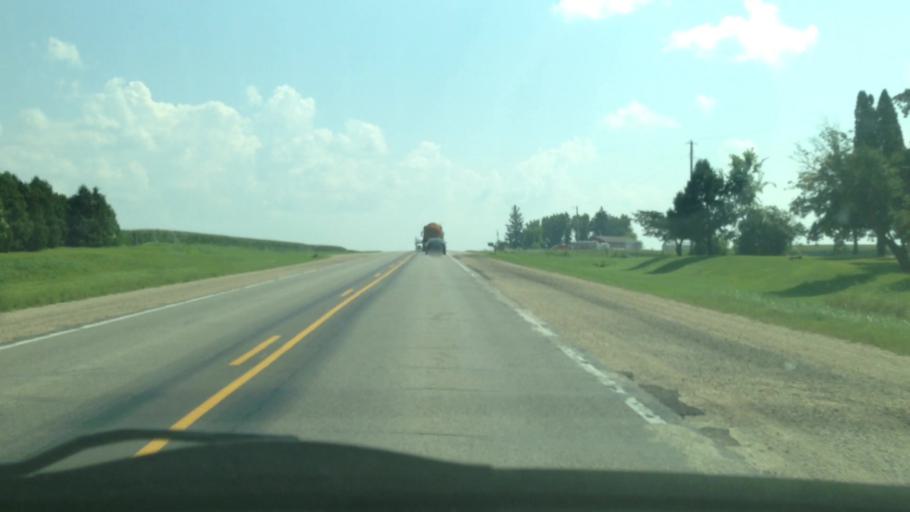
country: US
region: Iowa
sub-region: Chickasaw County
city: New Hampton
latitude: 43.2224
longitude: -92.2987
